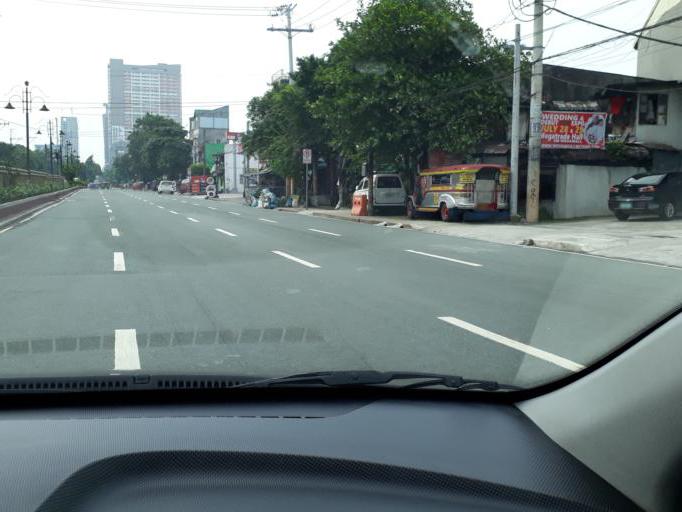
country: PH
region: Metro Manila
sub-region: City of Manila
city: Quiapo
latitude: 14.6052
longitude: 120.9970
